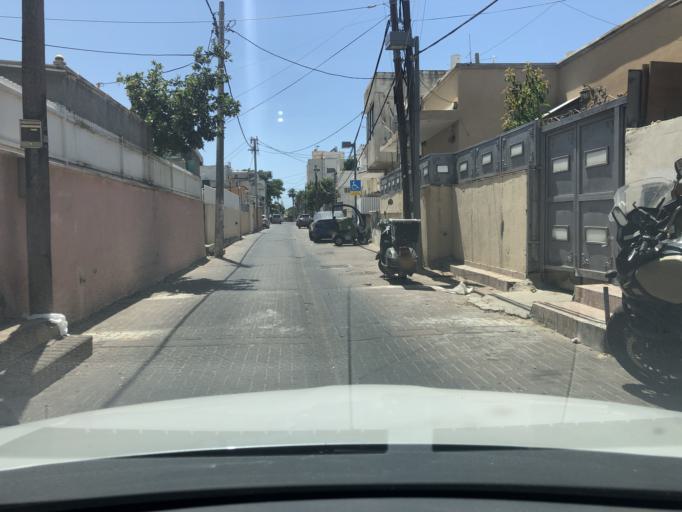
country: IL
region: Tel Aviv
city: Azor
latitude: 32.0463
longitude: 34.7936
